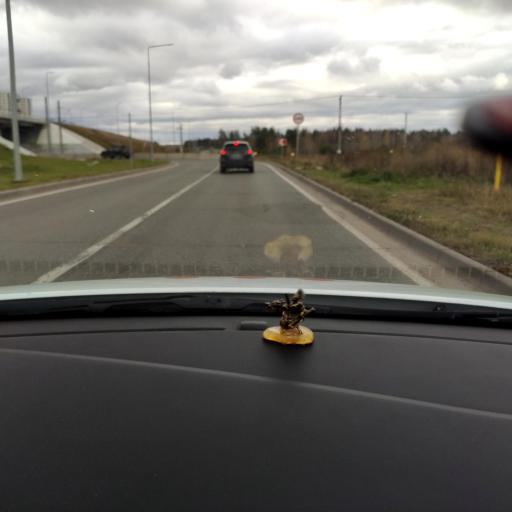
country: RU
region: Tatarstan
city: Stolbishchi
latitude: 55.6848
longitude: 49.2028
